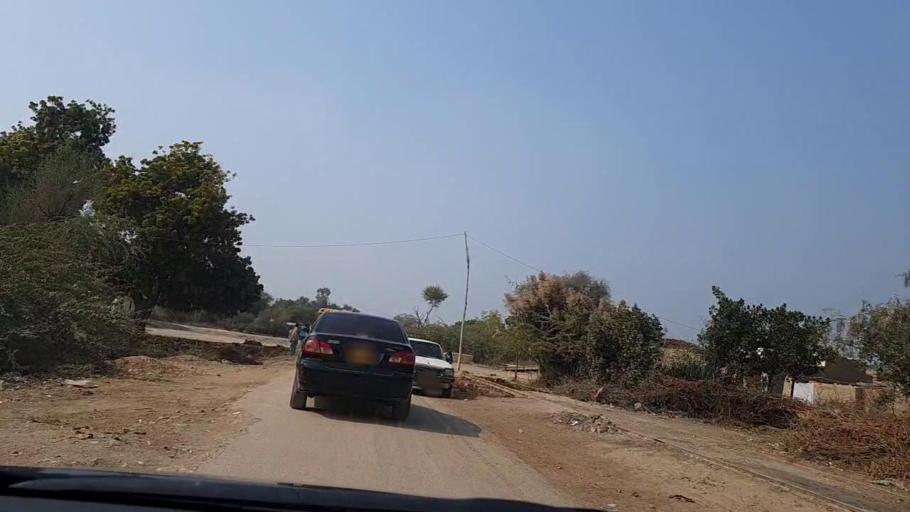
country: PK
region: Sindh
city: Sakrand
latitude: 26.1434
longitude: 68.2713
